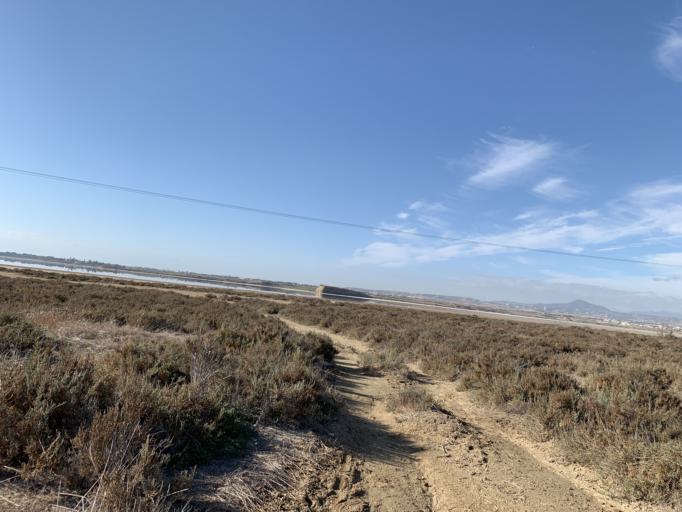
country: CY
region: Larnaka
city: Larnaca
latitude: 34.9023
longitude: 33.6228
